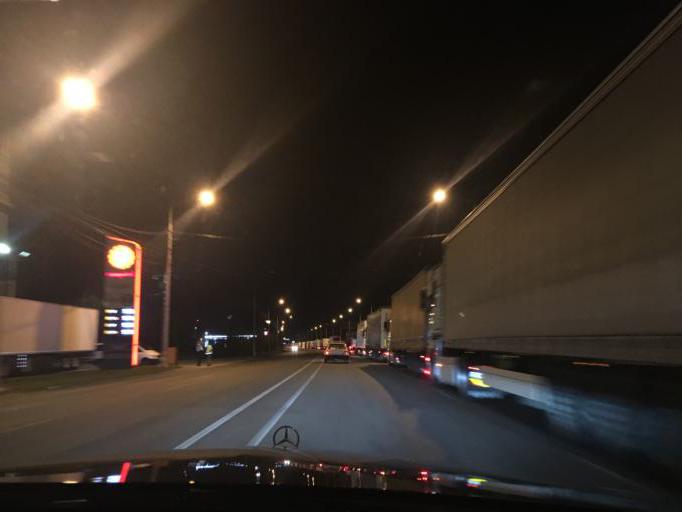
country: RO
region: Bihor
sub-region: Comuna Bors
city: Bors
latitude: 47.1131
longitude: 21.8110
